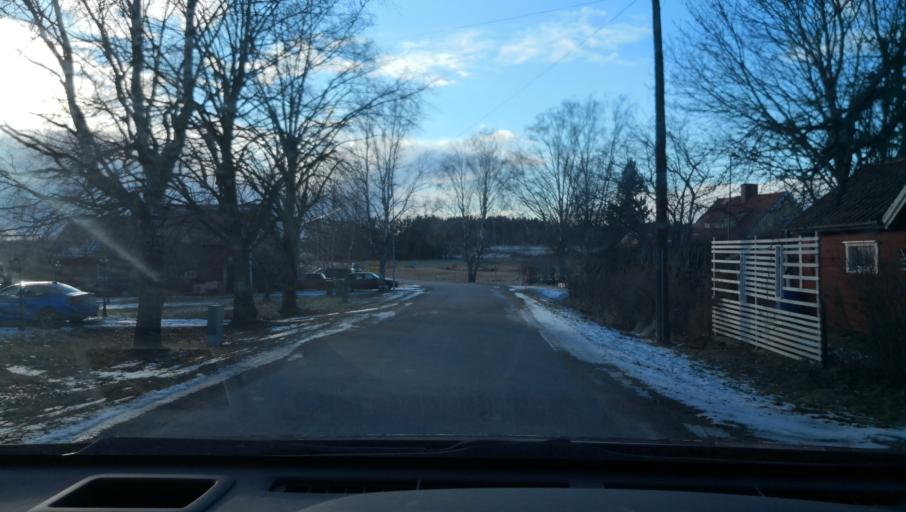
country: SE
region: Uppsala
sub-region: Enkopings Kommun
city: Irsta
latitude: 59.6613
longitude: 16.8291
